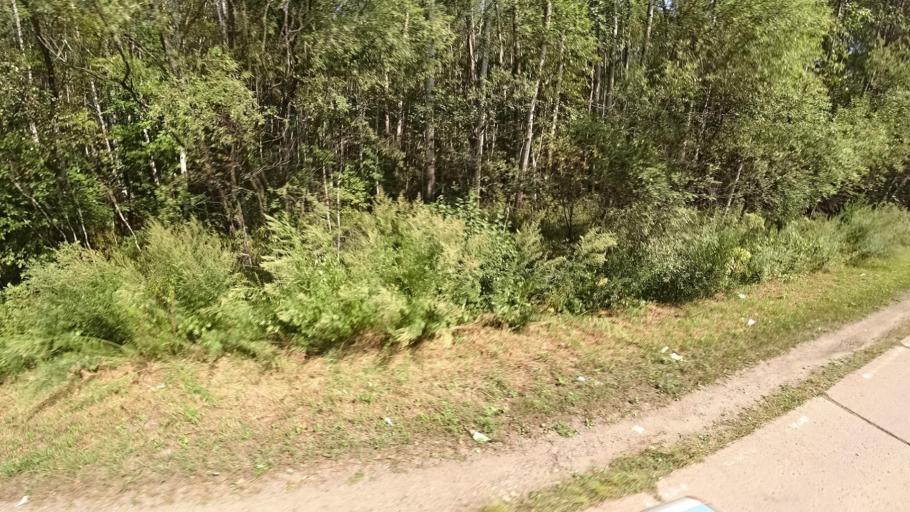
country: RU
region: Khabarovsk Krai
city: Khor
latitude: 47.9909
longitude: 135.0942
